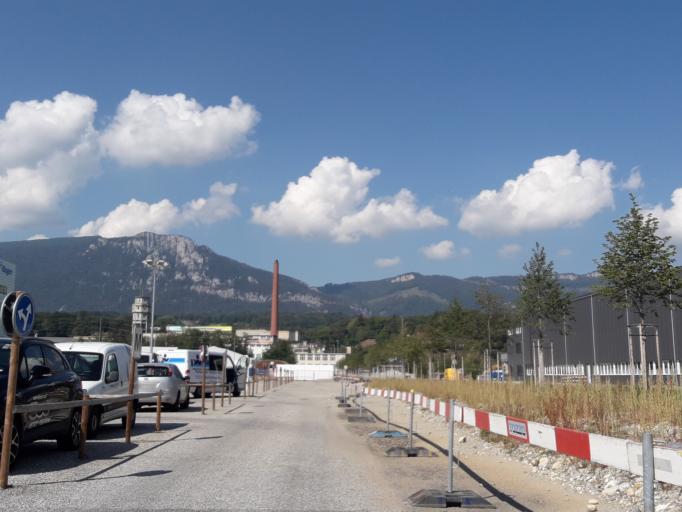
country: CH
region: Solothurn
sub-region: Bezirk Wasseramt
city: Luterbach
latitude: 47.2212
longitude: 7.5820
